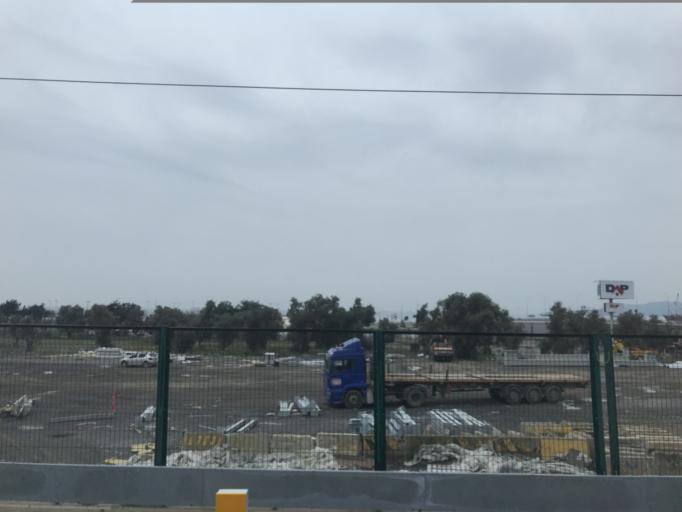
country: TR
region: Istanbul
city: Pendik
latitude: 40.8840
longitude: 29.2112
